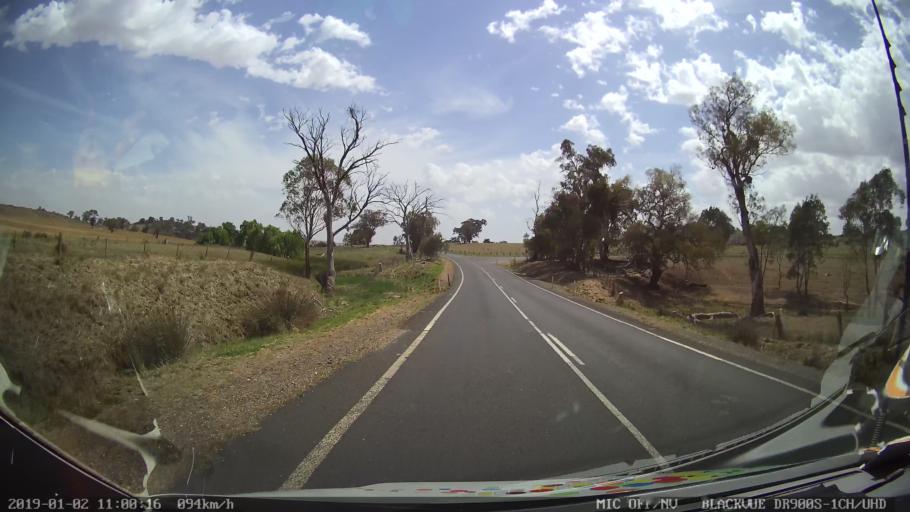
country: AU
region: New South Wales
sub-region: Cootamundra
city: Cootamundra
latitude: -34.6062
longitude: 148.3129
